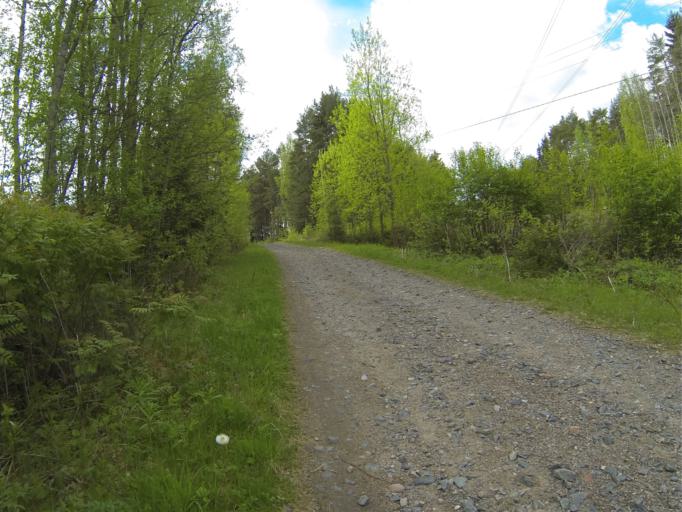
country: FI
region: Varsinais-Suomi
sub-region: Salo
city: Salo
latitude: 60.3559
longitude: 23.1167
